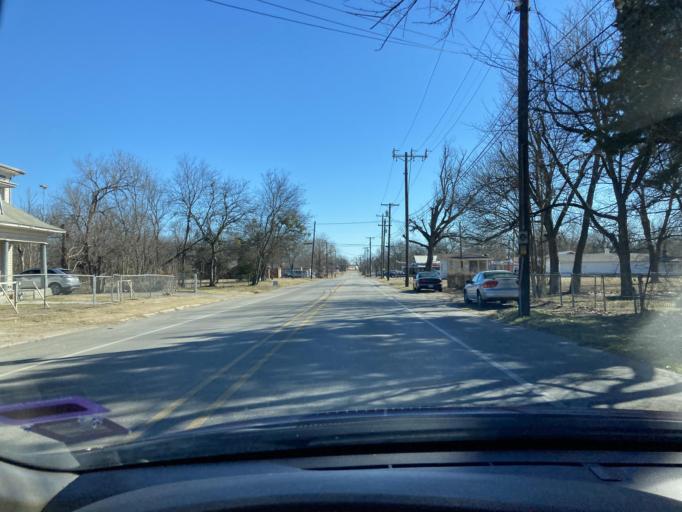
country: US
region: Texas
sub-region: Navarro County
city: Corsicana
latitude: 32.0858
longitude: -96.4655
